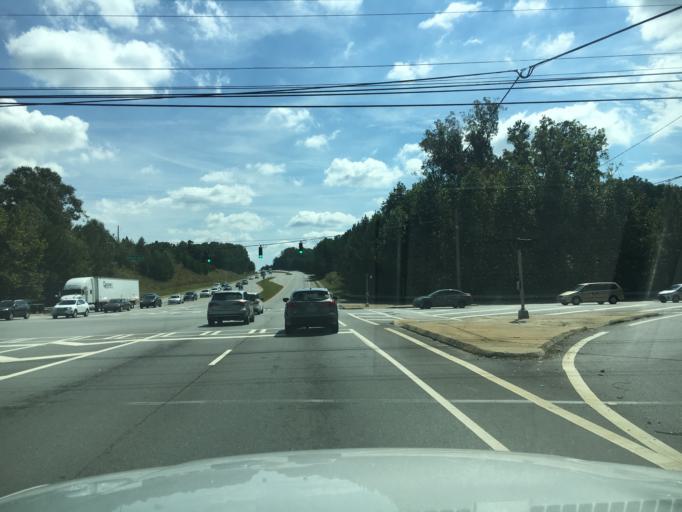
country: US
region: Georgia
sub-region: Gwinnett County
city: Duluth
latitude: 34.0201
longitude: -84.1176
